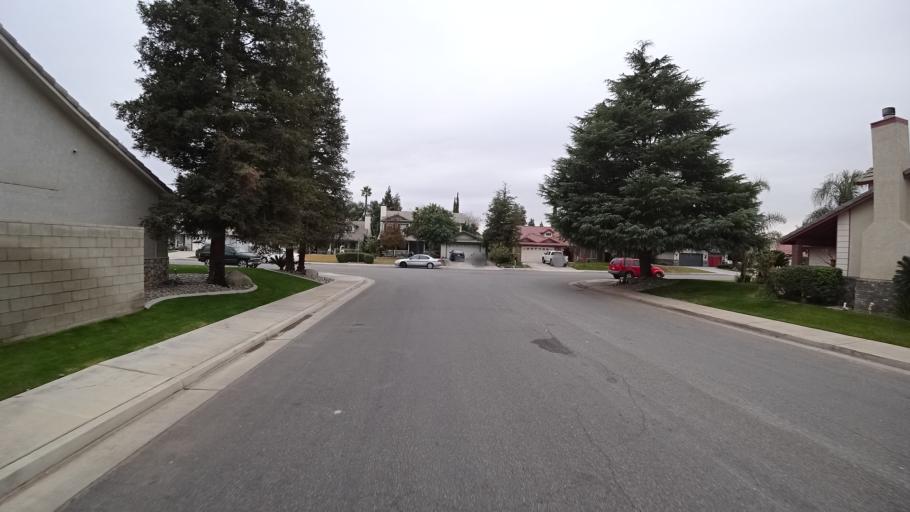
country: US
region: California
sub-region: Kern County
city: Greenfield
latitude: 35.2883
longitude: -119.0409
